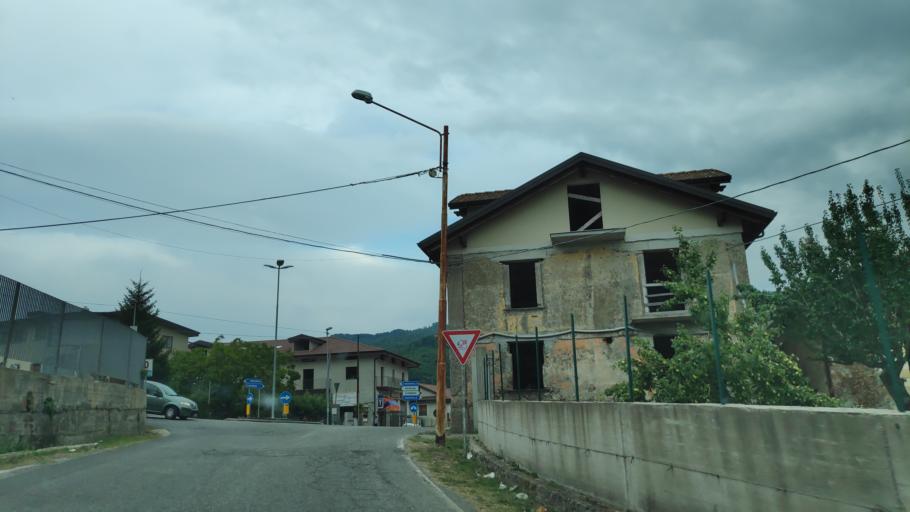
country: IT
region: Calabria
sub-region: Provincia di Catanzaro
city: Cardinale
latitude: 38.6466
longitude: 16.3820
